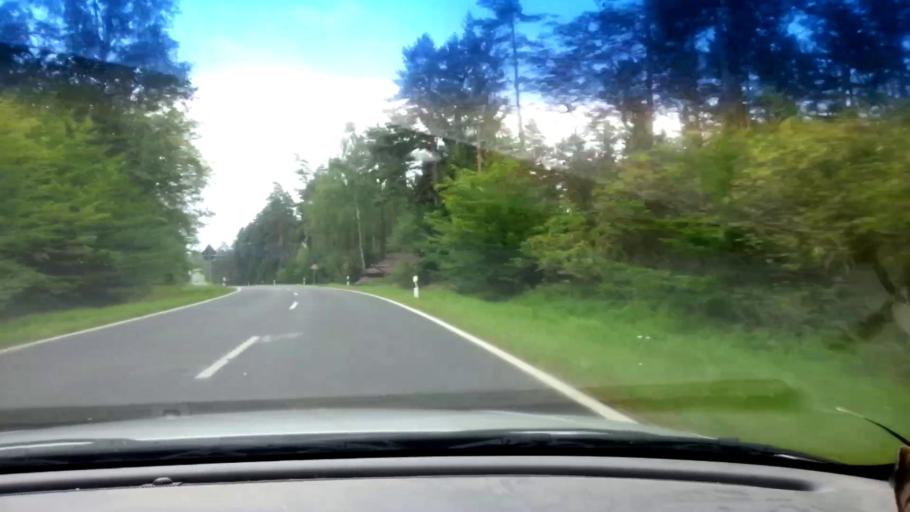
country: DE
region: Bavaria
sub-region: Upper Franconia
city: Schirnding
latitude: 50.0715
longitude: 12.2407
